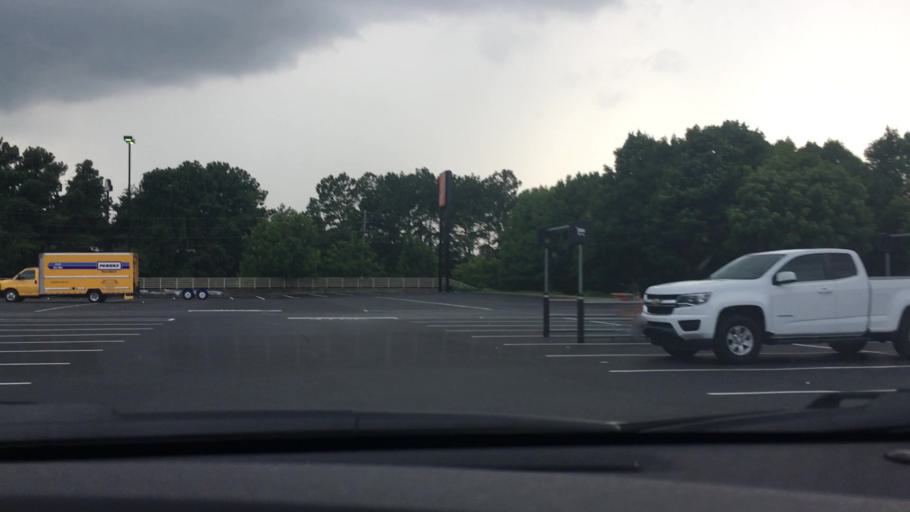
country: US
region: Georgia
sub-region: Cobb County
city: Kennesaw
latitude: 34.0074
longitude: -84.5640
